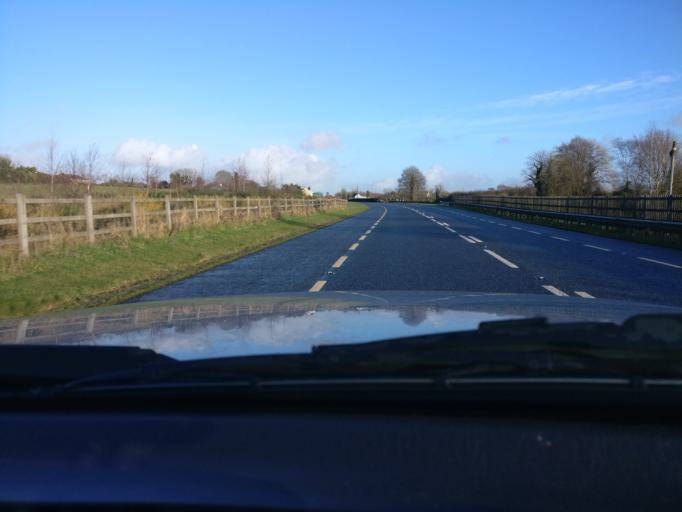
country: IE
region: Leinster
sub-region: An Iarmhi
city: An Muileann gCearr
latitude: 53.5496
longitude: -7.2800
